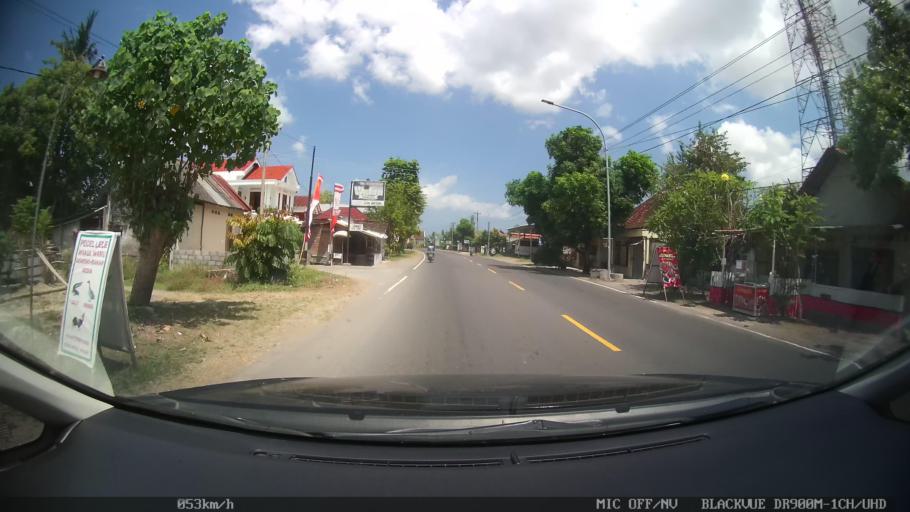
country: ID
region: Daerah Istimewa Yogyakarta
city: Sewon
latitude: -7.8856
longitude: 110.3467
